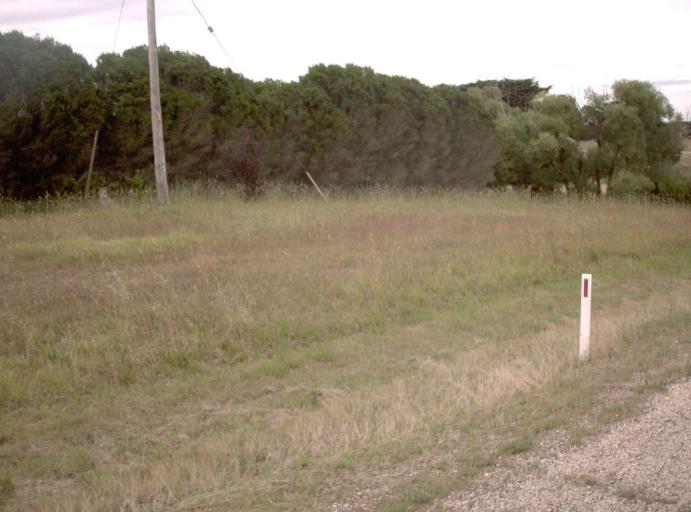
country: AU
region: Victoria
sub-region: East Gippsland
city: Bairnsdale
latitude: -37.8177
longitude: 147.4937
